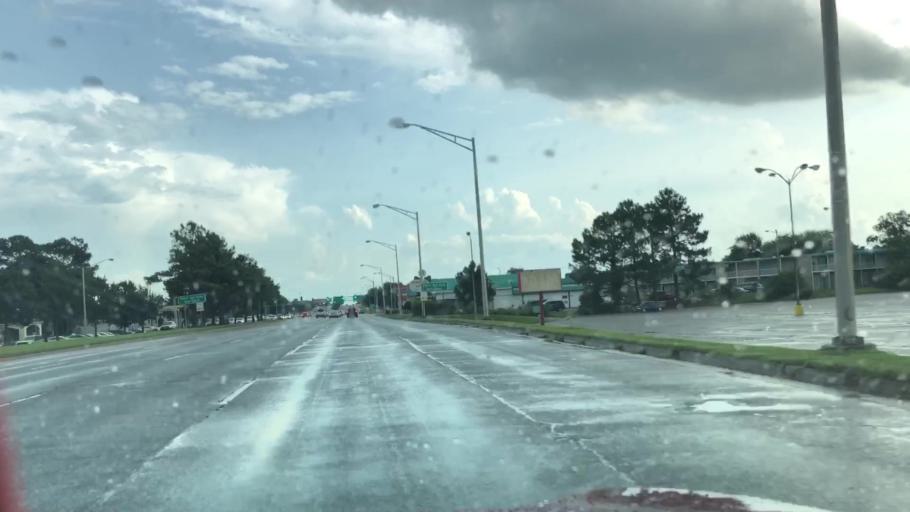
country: US
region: Virginia
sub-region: City of Chesapeake
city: Chesapeake
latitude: 36.8513
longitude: -76.2102
